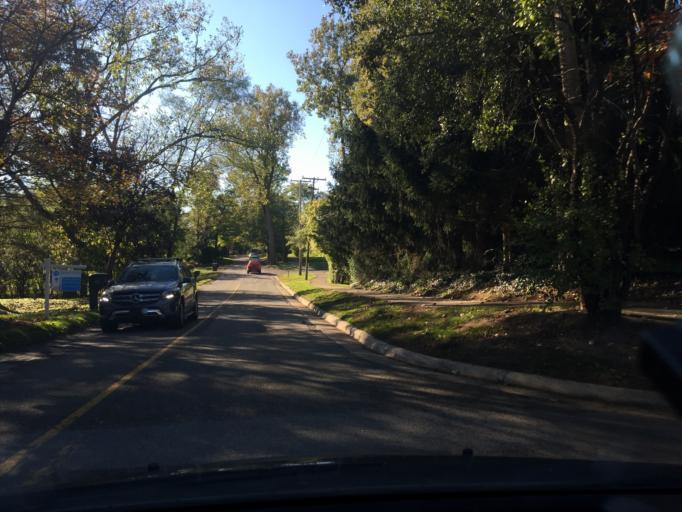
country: US
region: Michigan
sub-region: Oakland County
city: Bloomfield Hills
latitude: 42.5963
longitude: -83.2602
